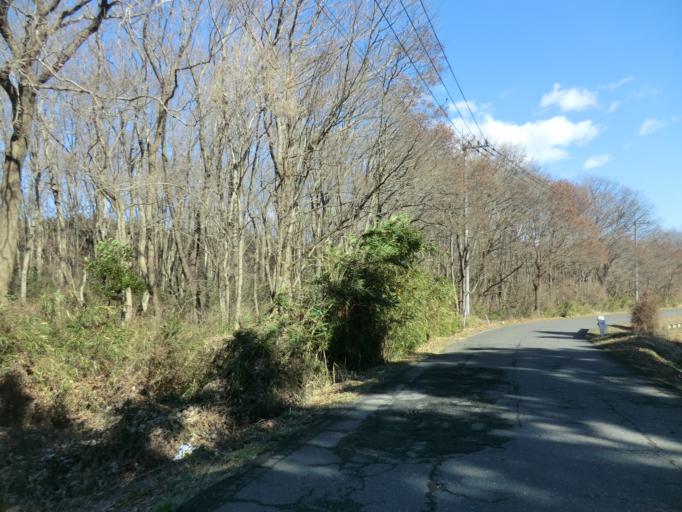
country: JP
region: Ibaraki
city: Tsukuba
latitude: 36.1971
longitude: 140.0386
